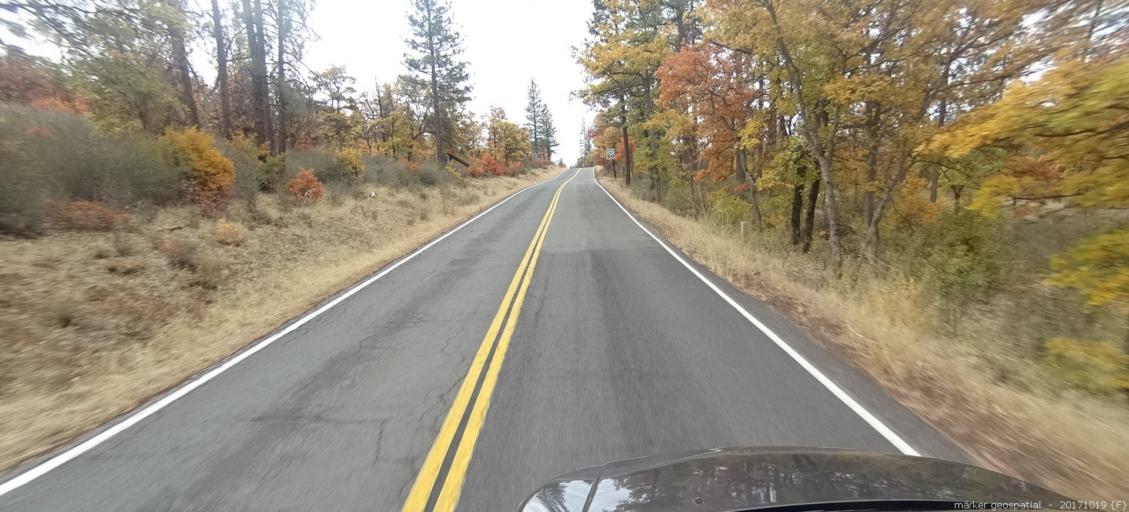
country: US
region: California
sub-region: Shasta County
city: Burney
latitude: 41.1535
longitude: -121.3538
